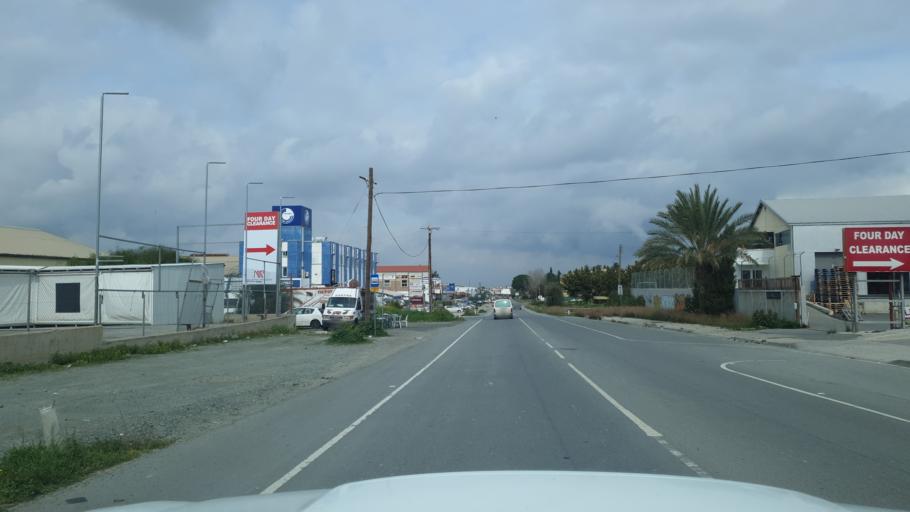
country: CY
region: Lefkosia
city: Geri
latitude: 35.0868
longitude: 33.3797
